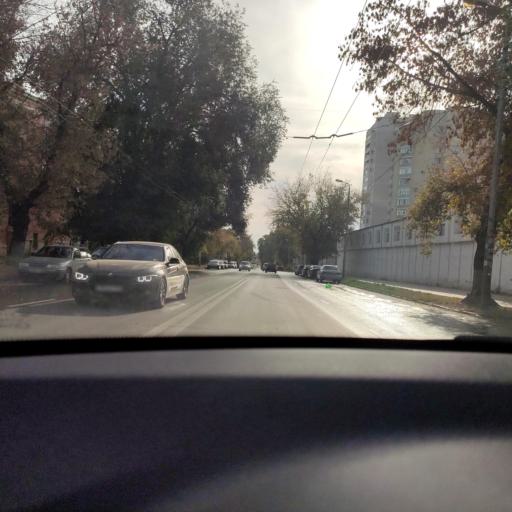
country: RU
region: Samara
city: Samara
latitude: 53.1860
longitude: 50.1084
